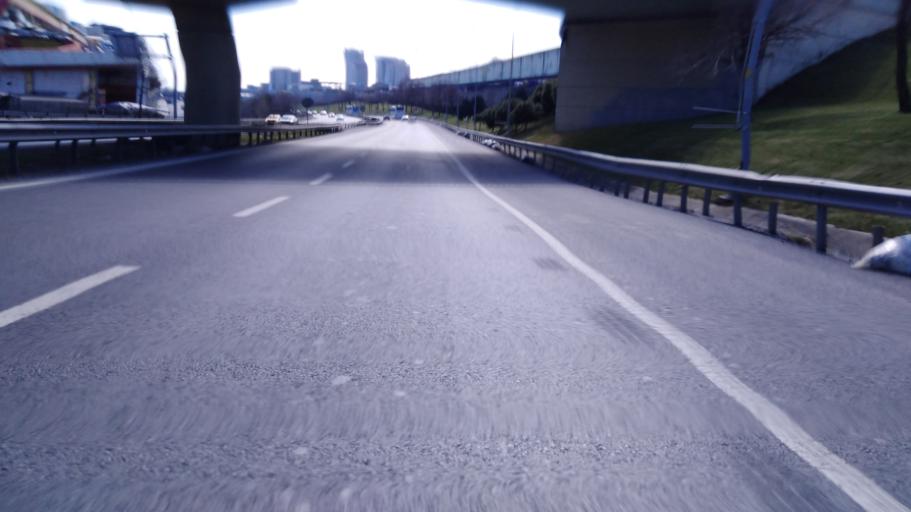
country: TR
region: Istanbul
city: Esenler
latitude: 41.0550
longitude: 28.8894
